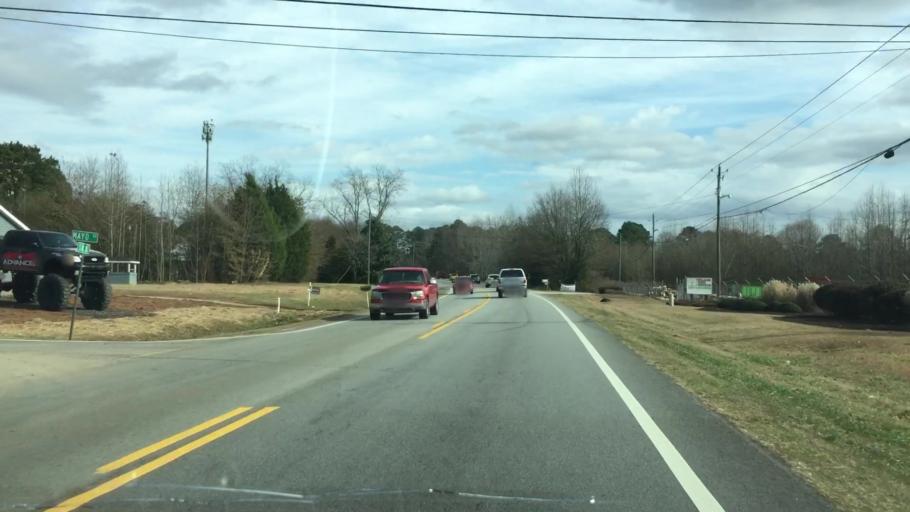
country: US
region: Georgia
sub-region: Henry County
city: McDonough
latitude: 33.4270
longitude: -84.0807
